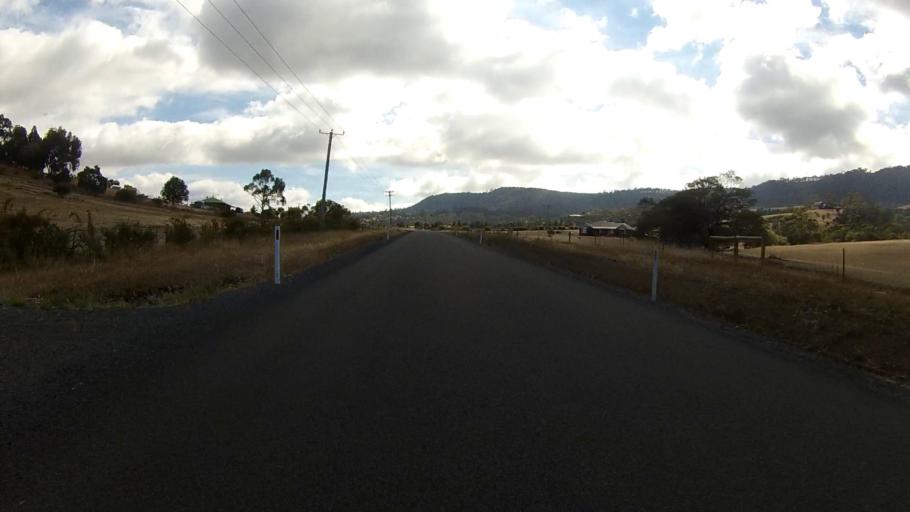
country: AU
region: Tasmania
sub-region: Brighton
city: Old Beach
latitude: -42.7673
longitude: 147.2978
